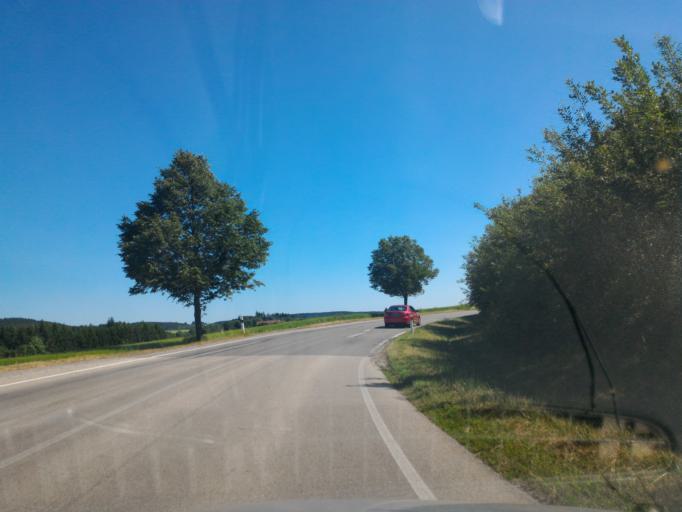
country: CZ
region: Vysocina
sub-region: Okres Jihlava
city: Trest'
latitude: 49.2798
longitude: 15.4771
